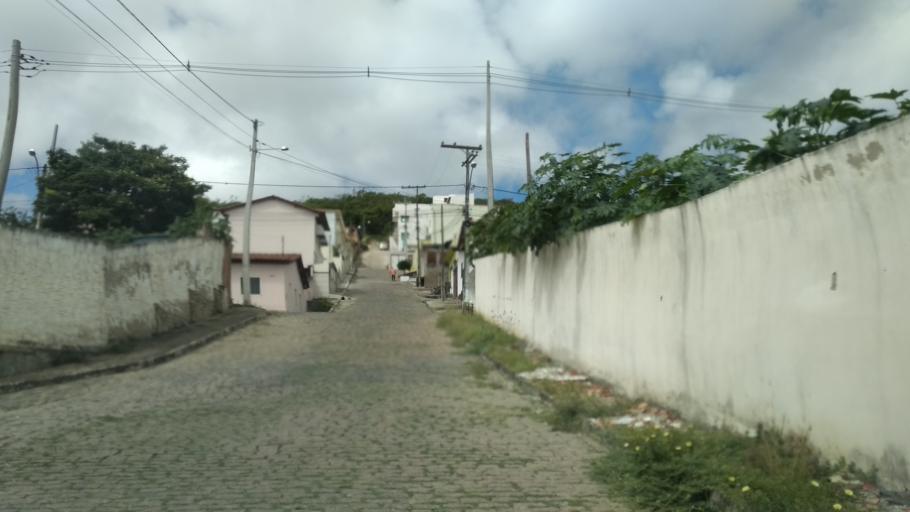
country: BR
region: Bahia
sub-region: Caetite
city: Caetite
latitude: -14.0683
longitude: -42.4949
